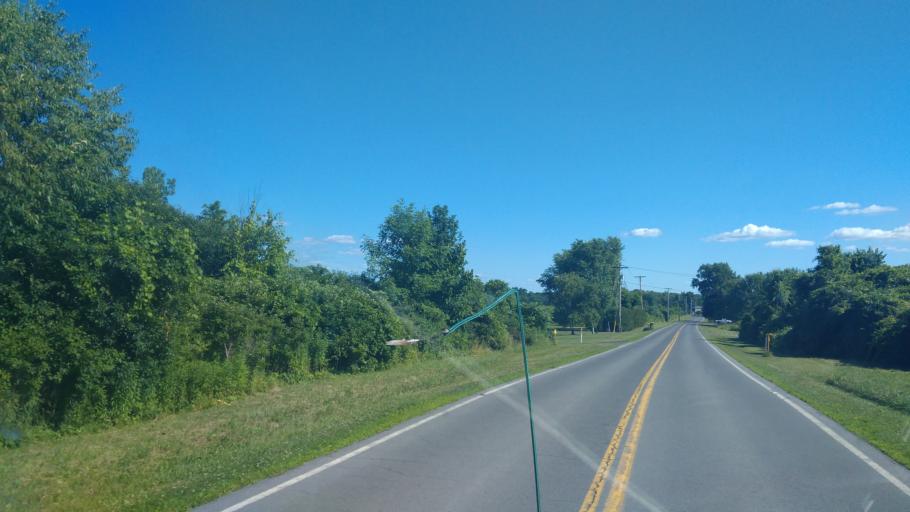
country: US
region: New York
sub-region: Seneca County
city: Seneca Falls
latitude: 42.9992
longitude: -76.8073
